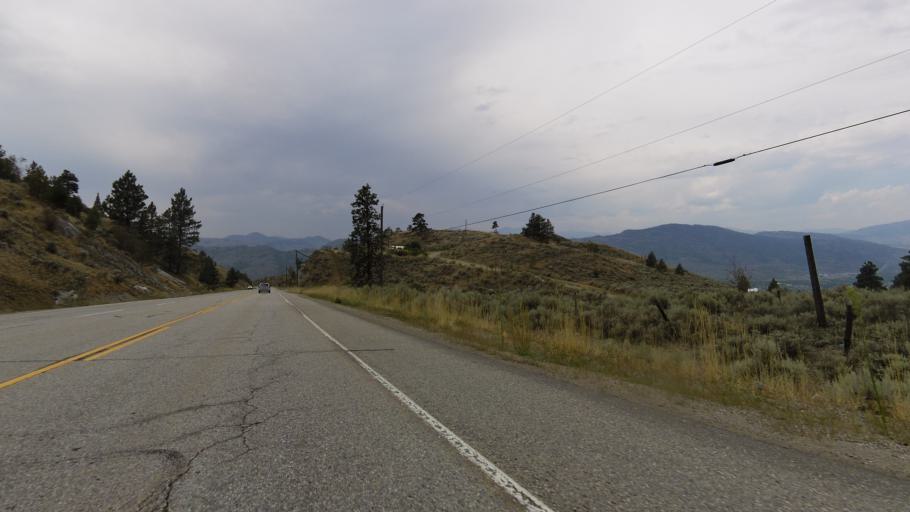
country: CA
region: British Columbia
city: Osoyoos
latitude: 49.0141
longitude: -119.4047
